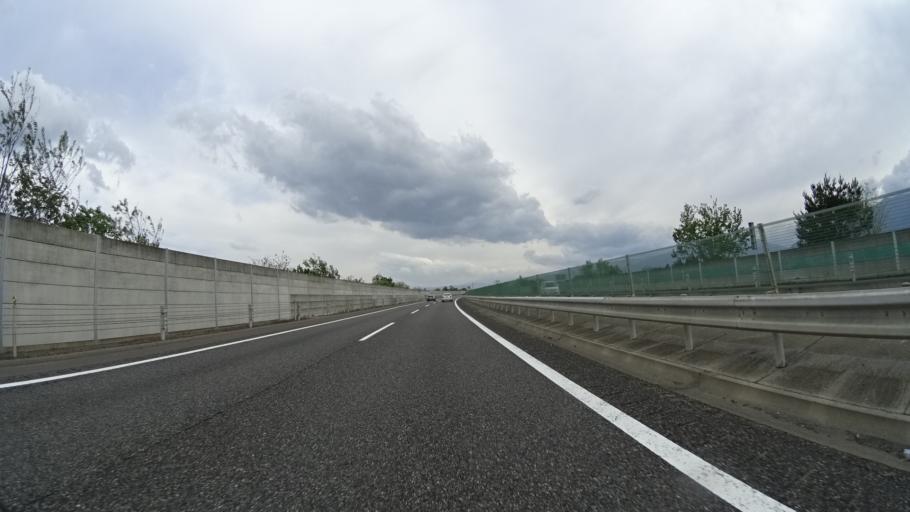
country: JP
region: Nagano
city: Toyoshina
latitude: 36.2793
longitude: 137.9315
